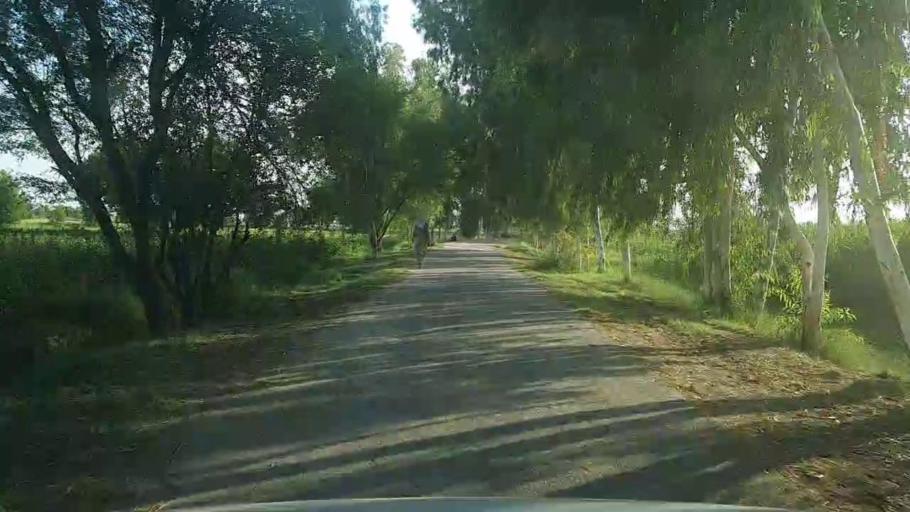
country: PK
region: Sindh
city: Khairpur
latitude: 28.0838
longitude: 69.6366
